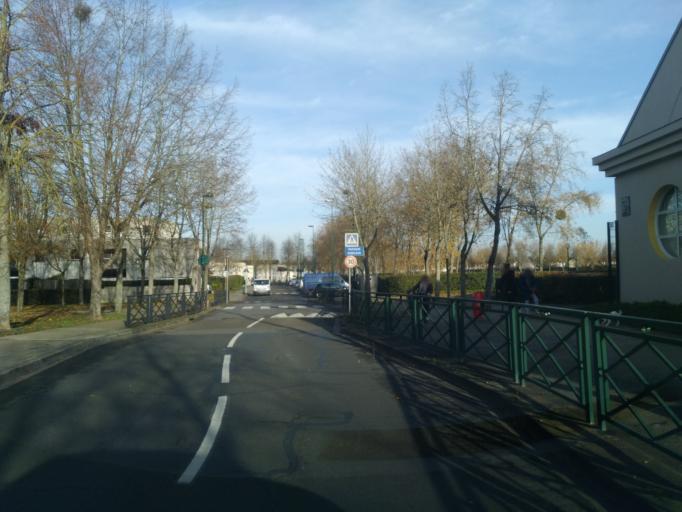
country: FR
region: Ile-de-France
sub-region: Departement des Yvelines
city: Plaisir
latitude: 48.8198
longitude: 1.9623
